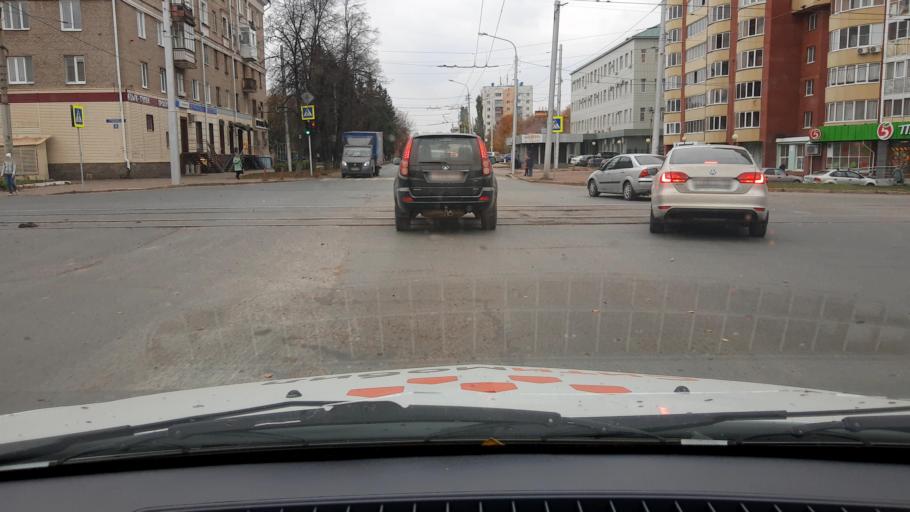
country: RU
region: Bashkortostan
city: Ufa
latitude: 54.8244
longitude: 56.0813
